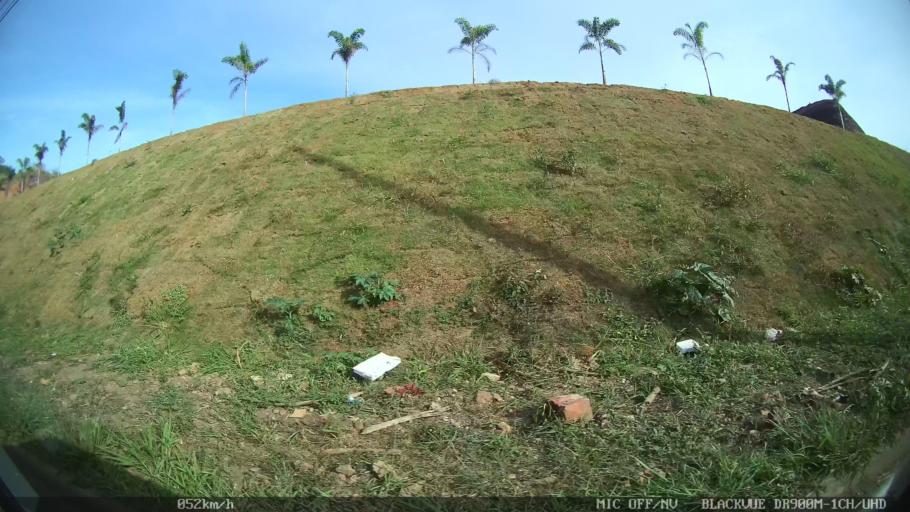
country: BR
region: Sao Paulo
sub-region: Piracicaba
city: Piracicaba
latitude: -22.7103
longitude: -47.6772
